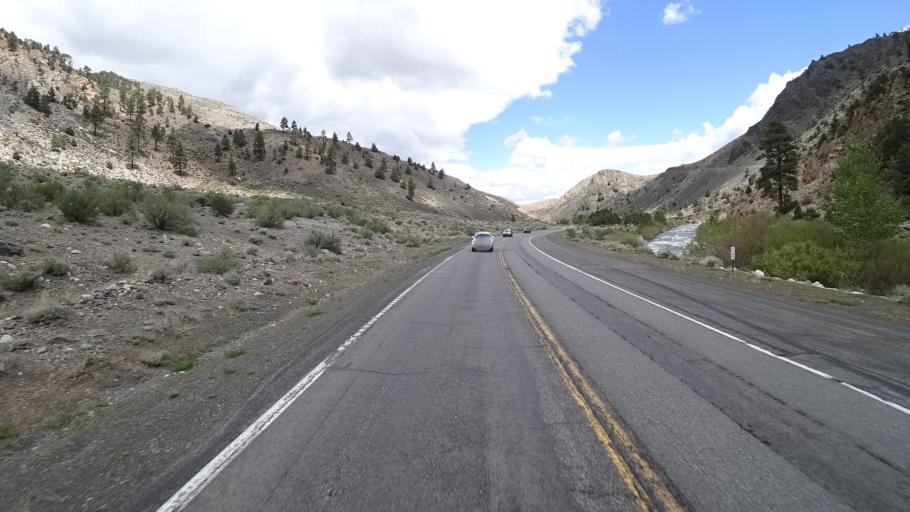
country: US
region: California
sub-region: Mono County
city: Bridgeport
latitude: 38.4732
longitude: -119.4622
